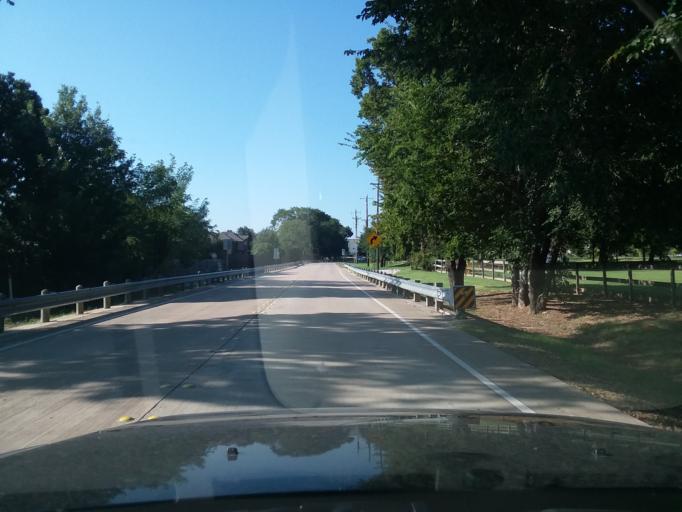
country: US
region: Texas
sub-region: Denton County
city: Copper Canyon
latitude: 33.0796
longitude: -97.0858
